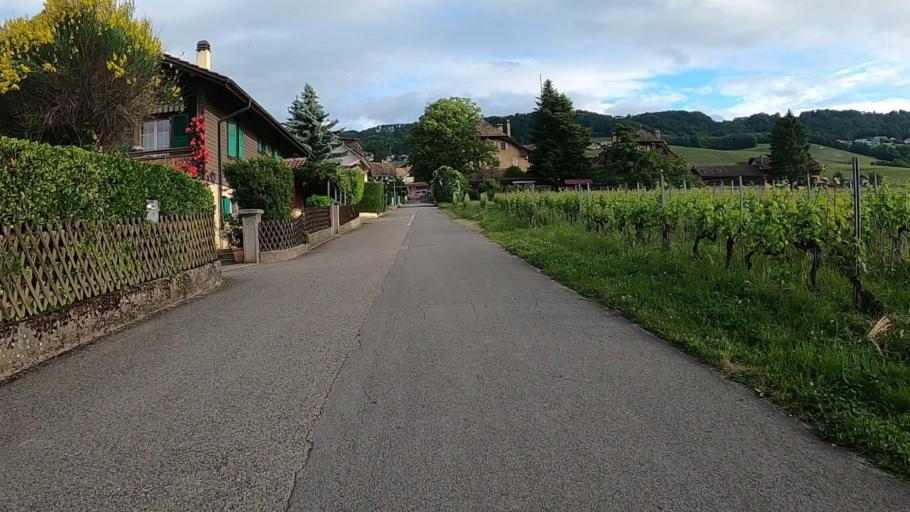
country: CH
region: Vaud
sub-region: Nyon District
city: Rolle
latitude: 46.4683
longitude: 6.3415
